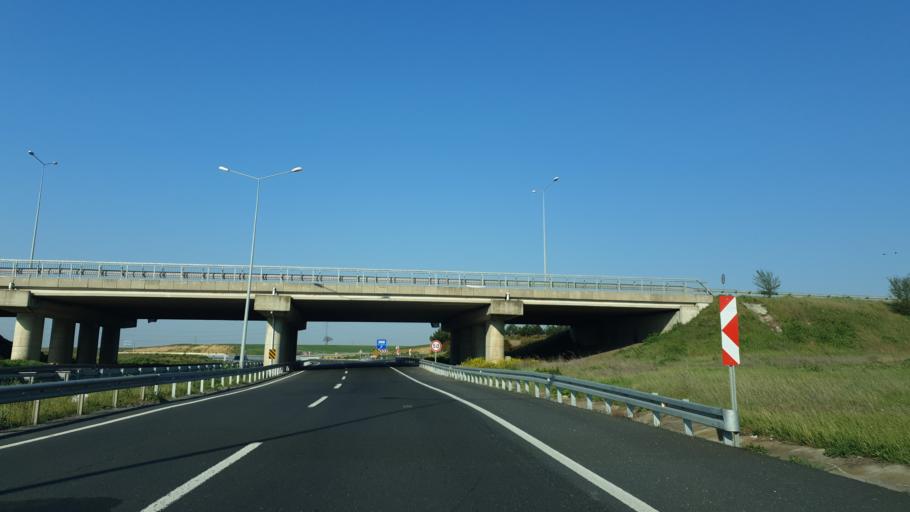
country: TR
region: Tekirdag
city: Marmaracik
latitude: 41.2001
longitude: 27.7595
